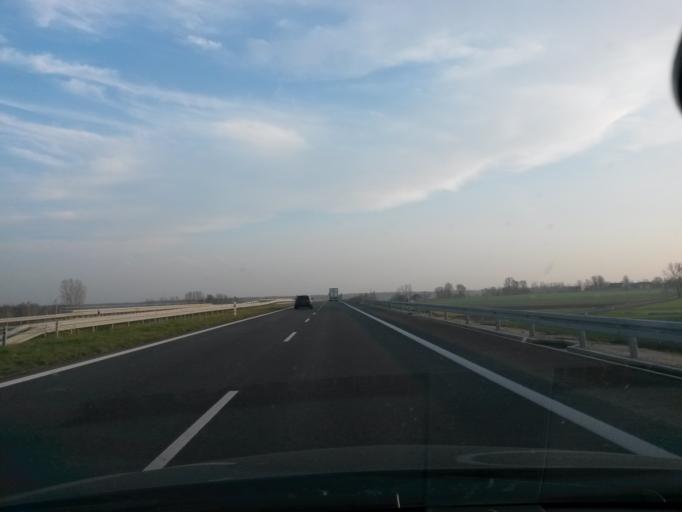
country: PL
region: Lodz Voivodeship
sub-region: Powiat wieruszowski
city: Wieruszow
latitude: 51.3280
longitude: 18.1506
